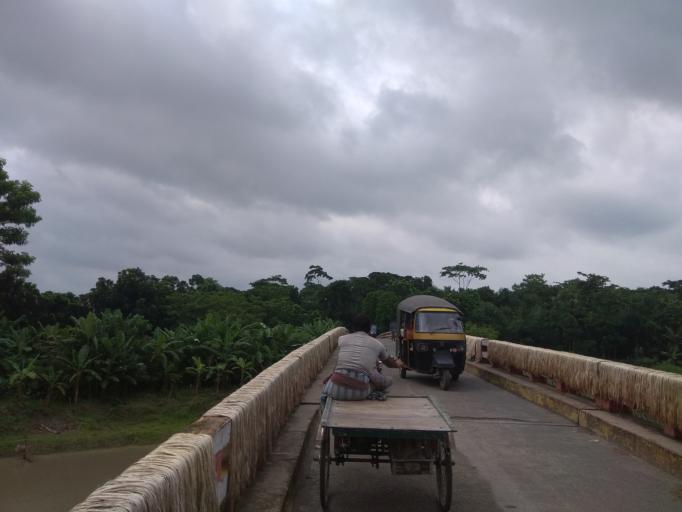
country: BD
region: Dhaka
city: Dohar
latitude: 23.4421
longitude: 90.0713
